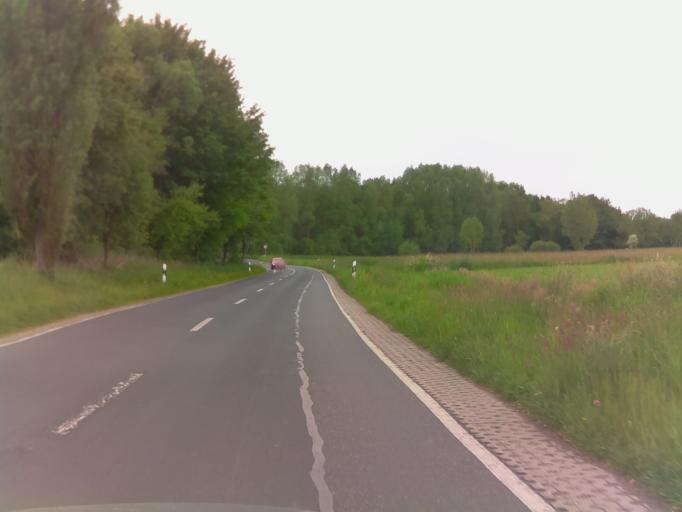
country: DE
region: Hesse
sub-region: Regierungsbezirk Kassel
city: Schrecksbach
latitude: 50.8830
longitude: 9.2609
